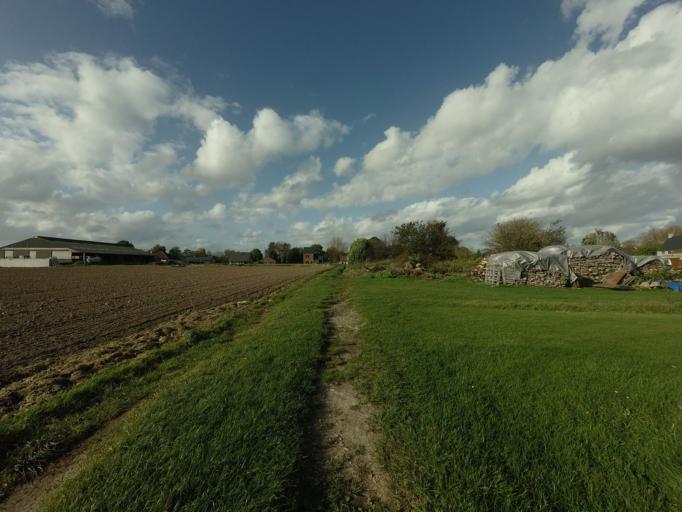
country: BE
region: Flanders
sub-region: Provincie Vlaams-Brabant
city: Zemst
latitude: 50.9985
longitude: 4.4450
